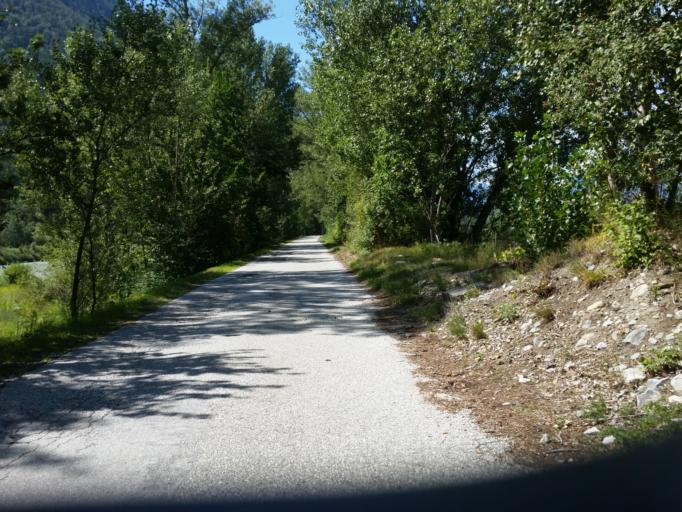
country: CH
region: Valais
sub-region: Conthey District
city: Basse-Nendaz
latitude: 46.2064
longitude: 7.3048
